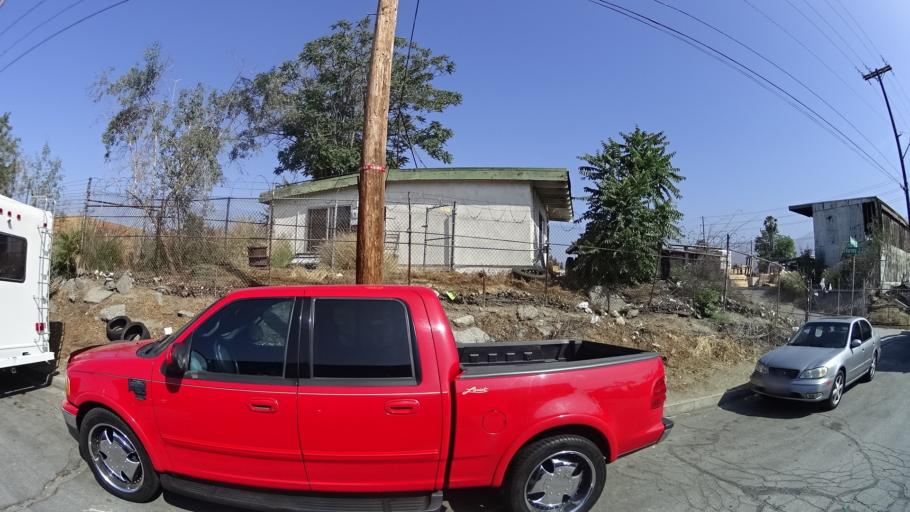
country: US
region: California
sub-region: Los Angeles County
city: Burbank
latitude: 34.1809
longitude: -118.3175
